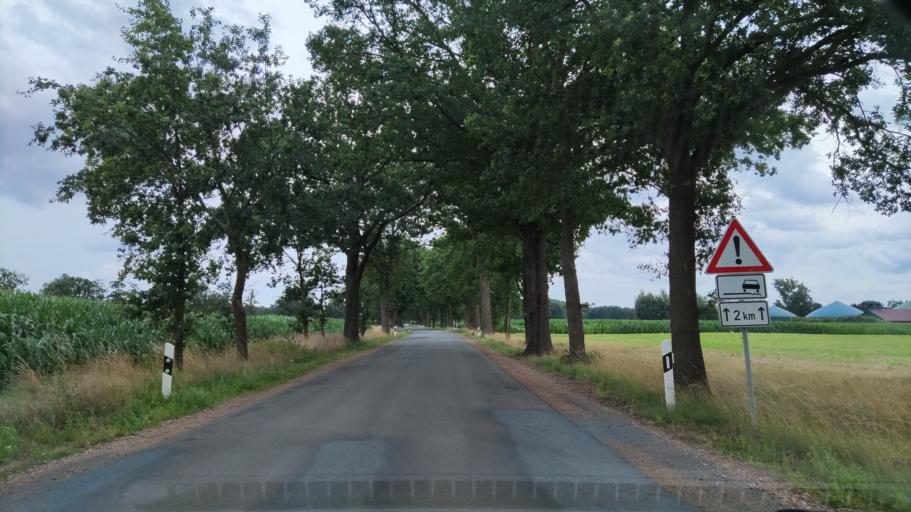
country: DE
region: Lower Saxony
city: Dannenberg
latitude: 53.0703
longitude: 11.1287
